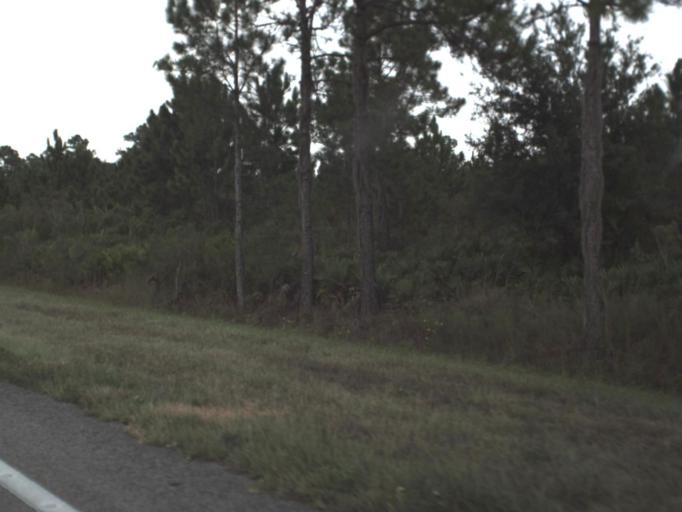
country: US
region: Florida
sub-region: Polk County
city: Frostproof
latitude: 27.7466
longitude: -81.5816
